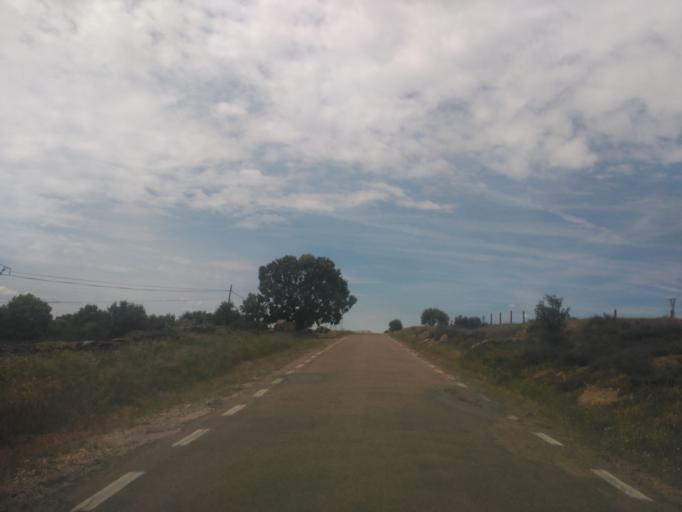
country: ES
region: Castille and Leon
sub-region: Provincia de Salamanca
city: Guijuelo
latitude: 40.5460
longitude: -5.6642
